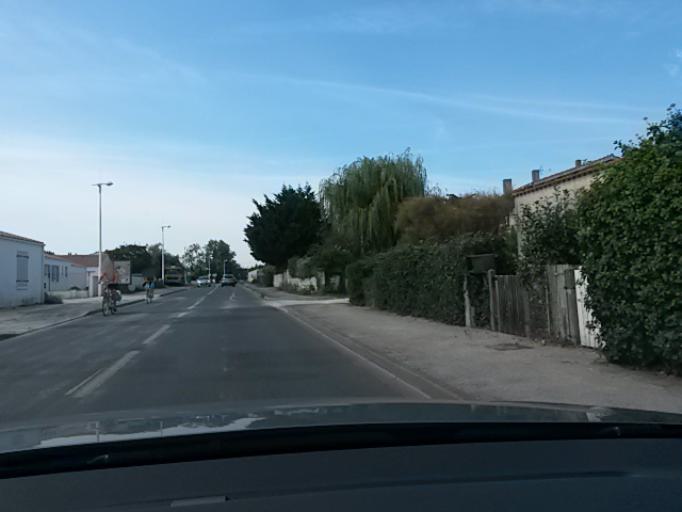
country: FR
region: Poitou-Charentes
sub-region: Departement de la Charente-Maritime
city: Dolus-d'Oleron
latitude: 45.9450
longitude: -1.3204
